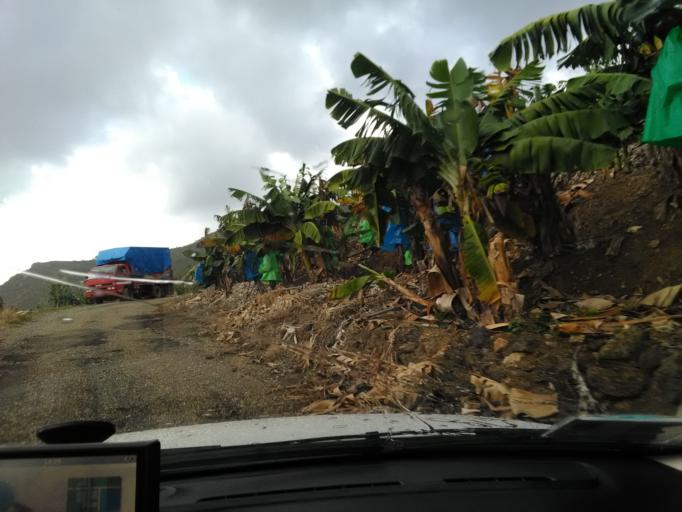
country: TR
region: Antalya
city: Gazipasa
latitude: 36.1589
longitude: 32.4199
